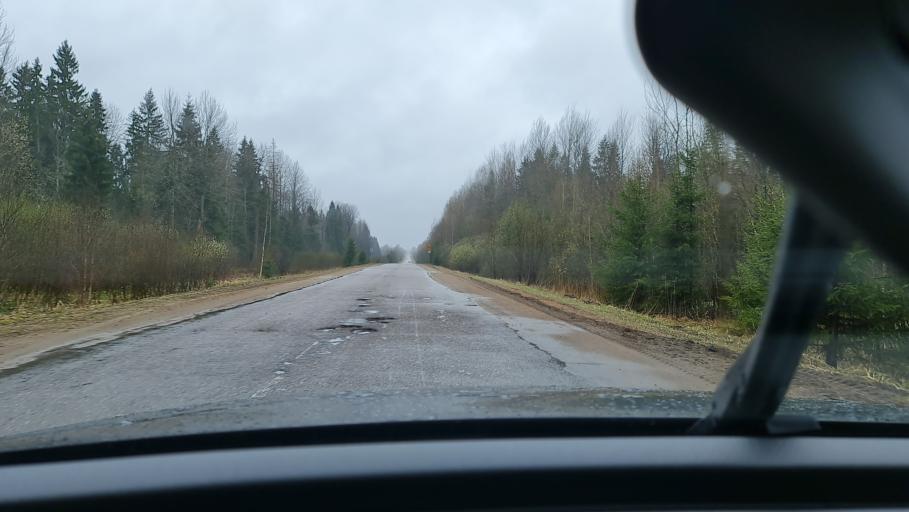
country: RU
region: Novgorod
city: Kresttsy
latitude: 58.0289
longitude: 32.8120
